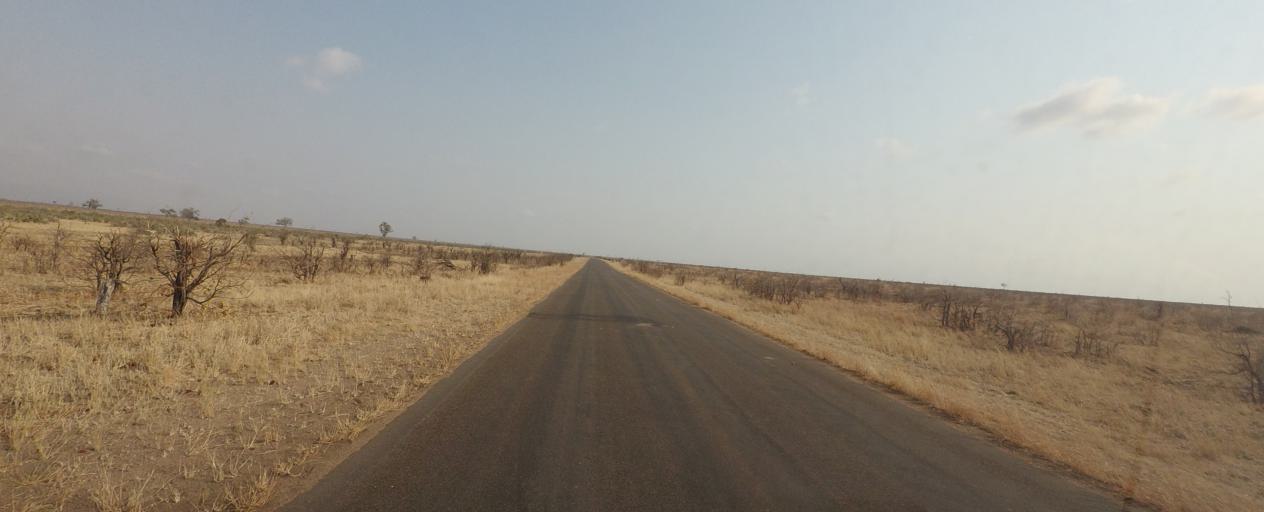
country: ZA
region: Limpopo
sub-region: Vhembe District Municipality
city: Mutale
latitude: -22.9504
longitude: 31.2881
